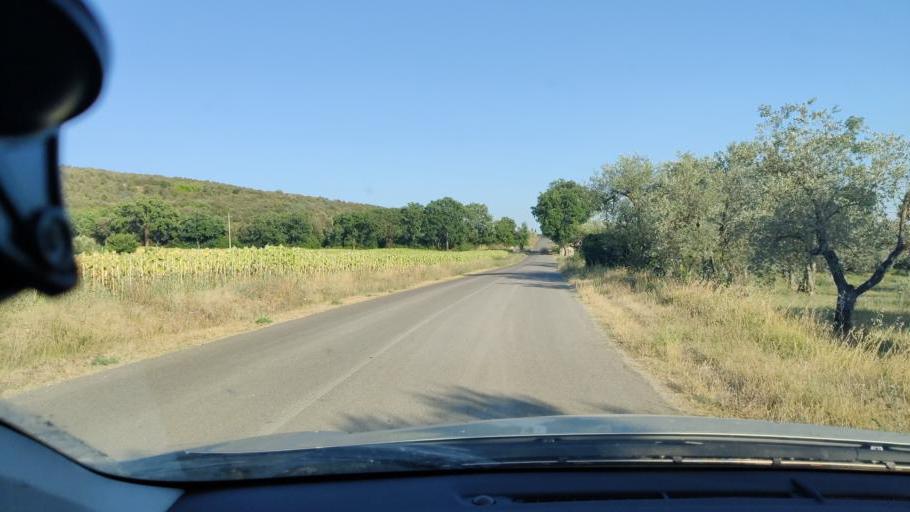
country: IT
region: Umbria
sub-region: Provincia di Terni
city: Lugnano in Teverina
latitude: 42.5479
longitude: 12.3492
